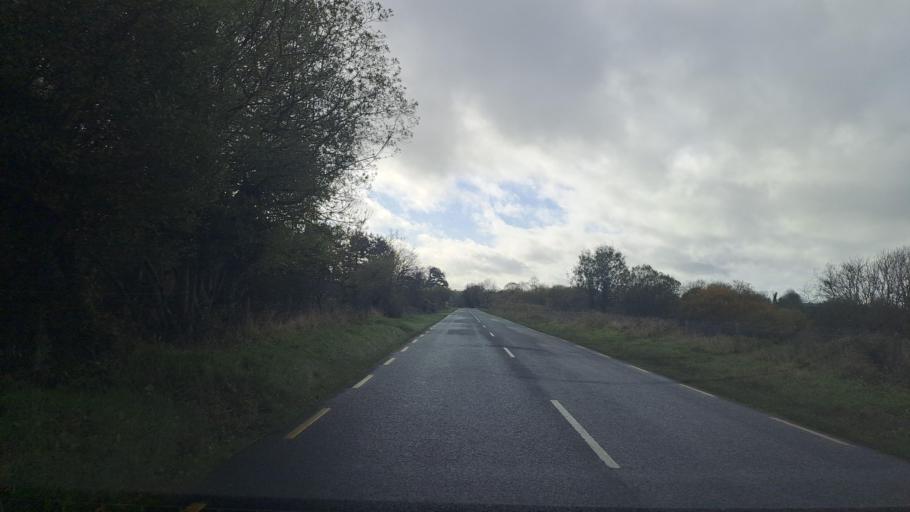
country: IE
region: Ulster
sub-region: County Monaghan
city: Monaghan
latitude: 54.1676
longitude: -6.9995
